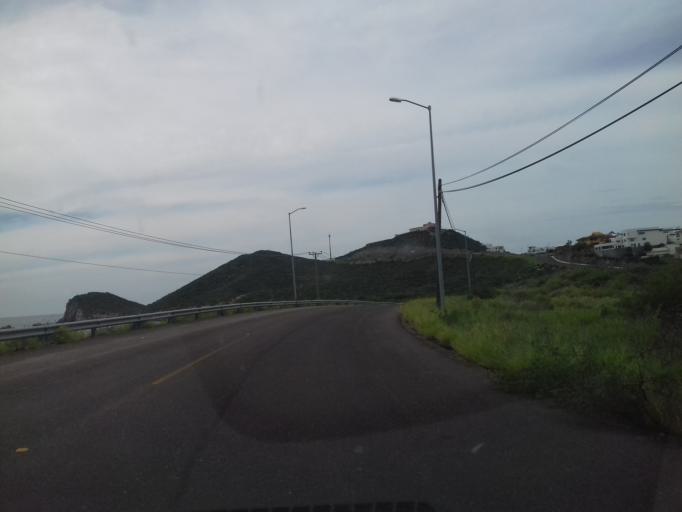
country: MX
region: Sonora
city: Heroica Guaymas
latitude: 27.9432
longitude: -111.0881
